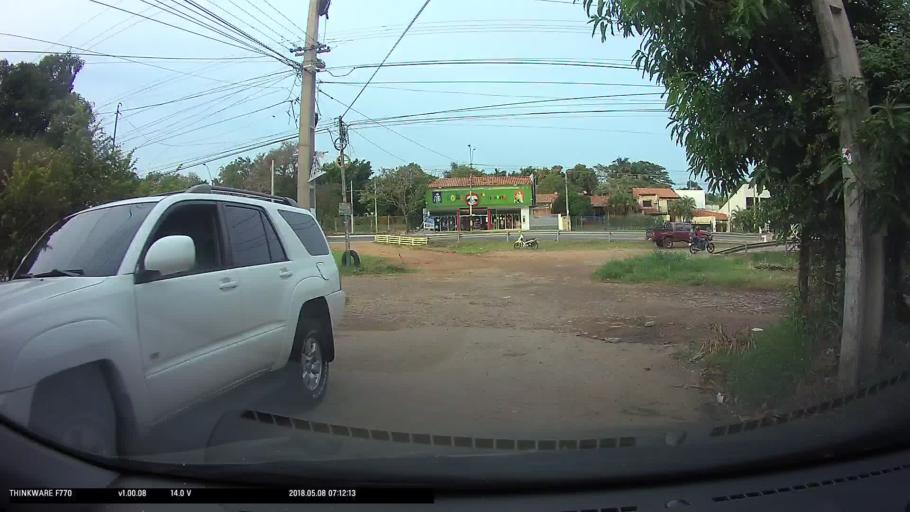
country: PY
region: Central
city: Fernando de la Mora
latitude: -25.2630
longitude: -57.5117
